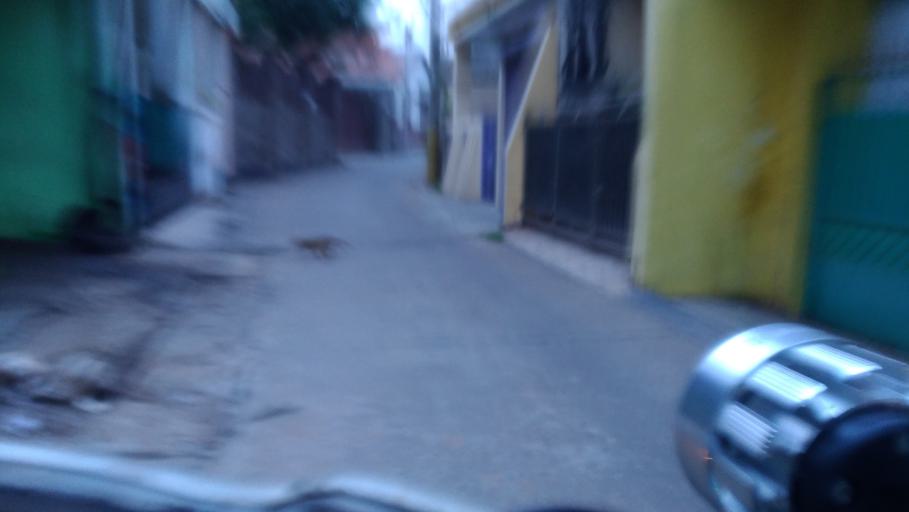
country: ID
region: West Java
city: Depok
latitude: -6.3527
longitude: 106.8777
